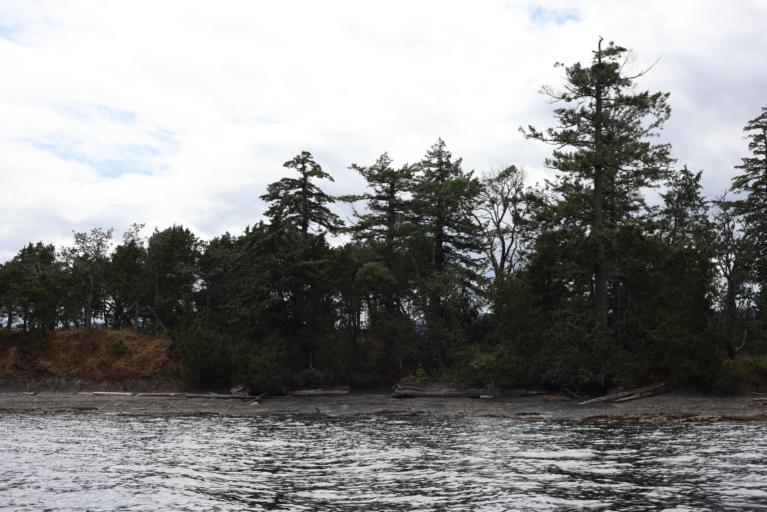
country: CA
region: British Columbia
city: North Cowichan
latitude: 48.8824
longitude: -123.6324
